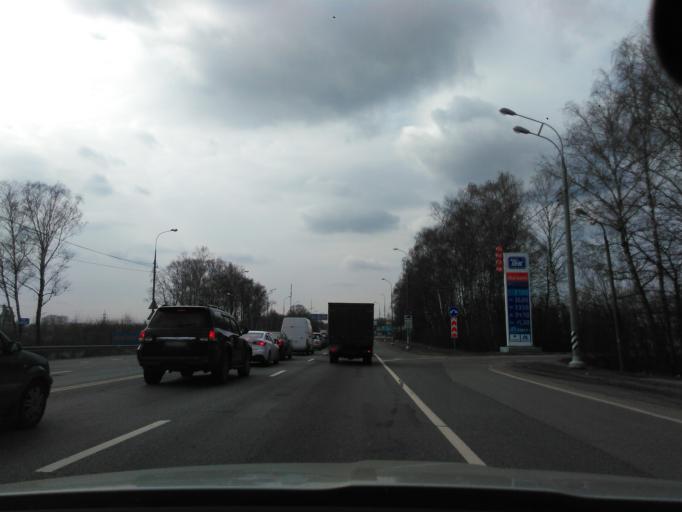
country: RU
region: Moskovskaya
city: Sheremet'yevskiy
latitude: 55.9964
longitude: 37.5352
